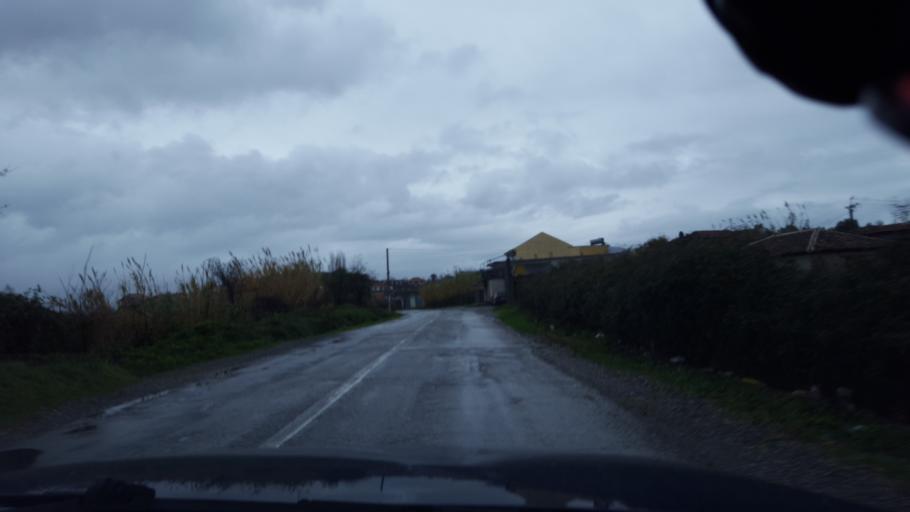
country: AL
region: Shkoder
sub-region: Rrethi i Shkodres
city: Berdica e Madhe
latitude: 42.0260
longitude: 19.4886
